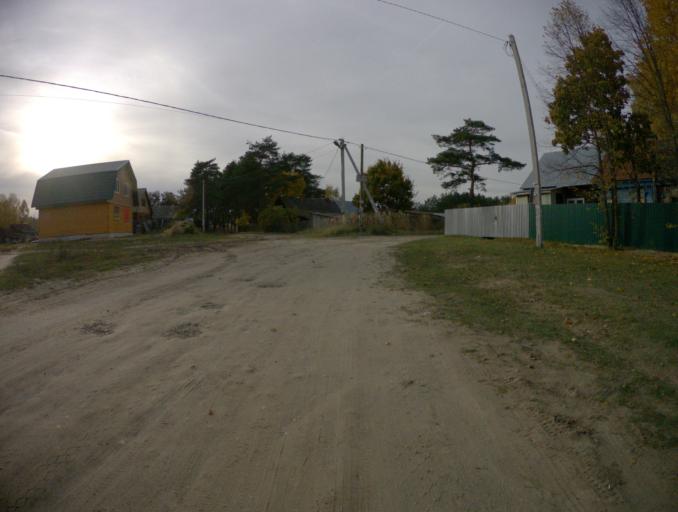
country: RU
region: Vladimir
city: Raduzhnyy
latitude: 56.0286
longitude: 40.3872
